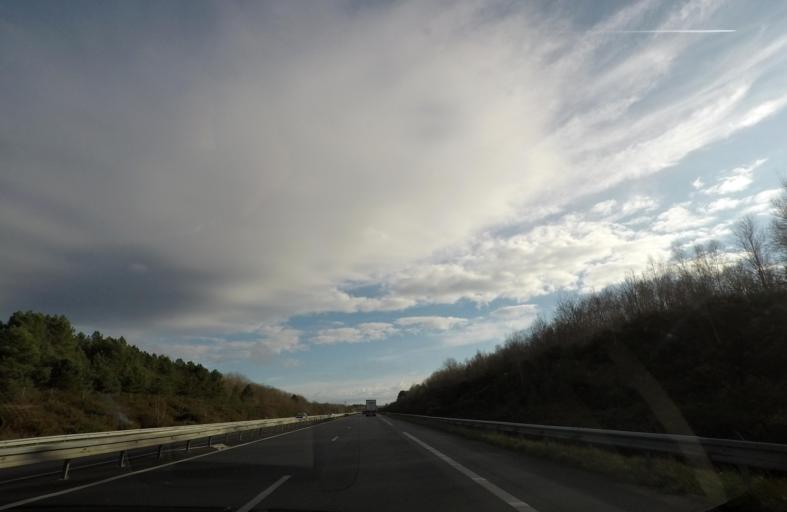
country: FR
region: Centre
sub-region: Departement du Loir-et-Cher
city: Villefranche-sur-Cher
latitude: 47.3099
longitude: 1.8361
